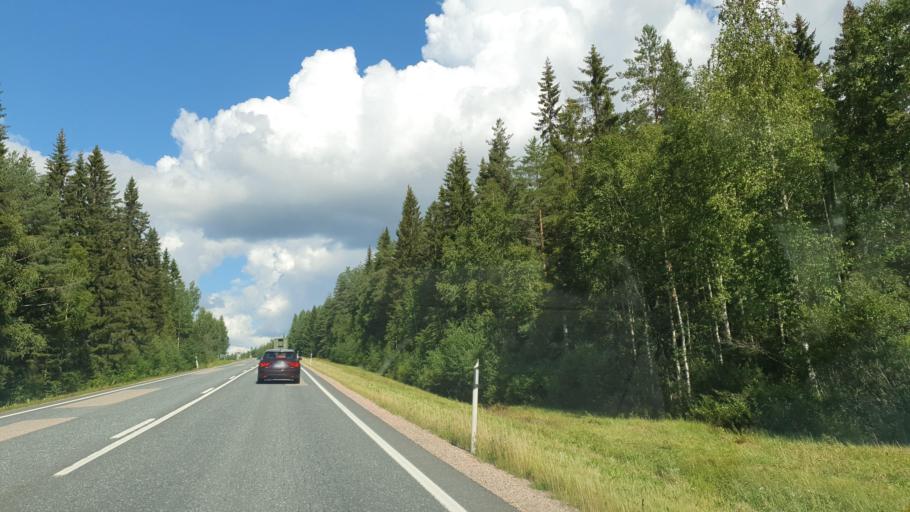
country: FI
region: Kainuu
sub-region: Kajaani
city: Kajaani
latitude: 64.0885
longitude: 27.4530
